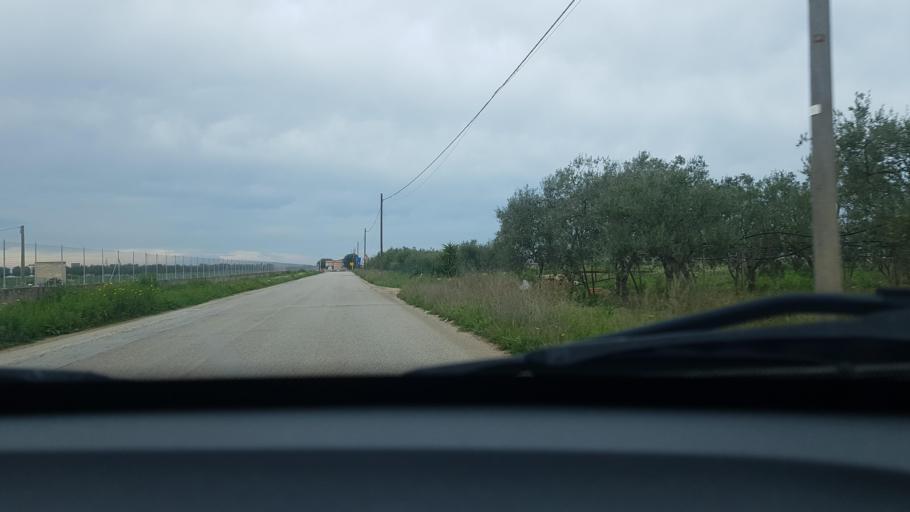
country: IT
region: Apulia
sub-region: Provincia di Bari
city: Noicattaro
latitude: 41.0363
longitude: 16.9714
